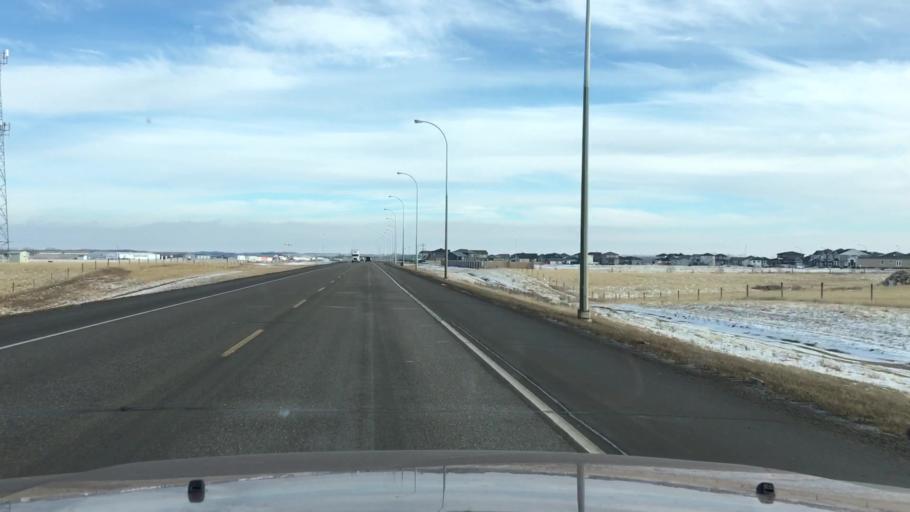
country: CA
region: Saskatchewan
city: Pilot Butte
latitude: 50.4868
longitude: -104.4263
